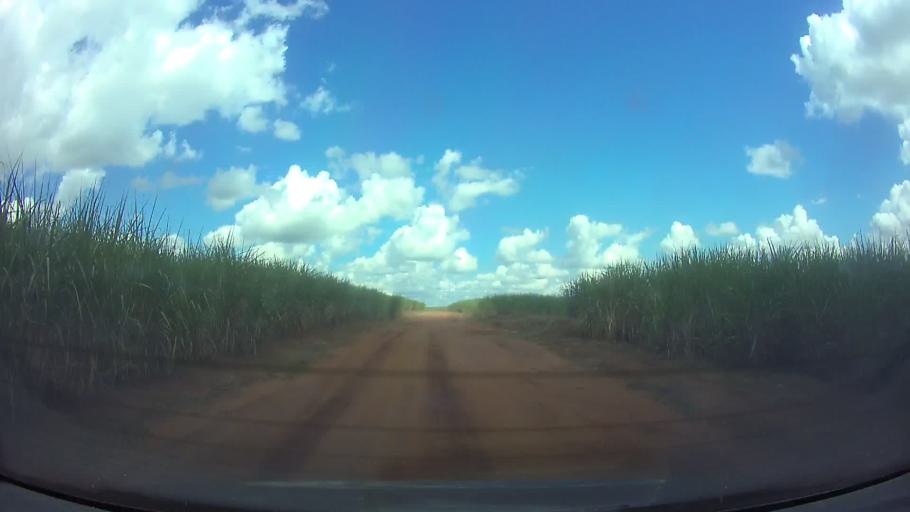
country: PY
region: Paraguari
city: La Colmena
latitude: -25.9525
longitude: -56.7670
